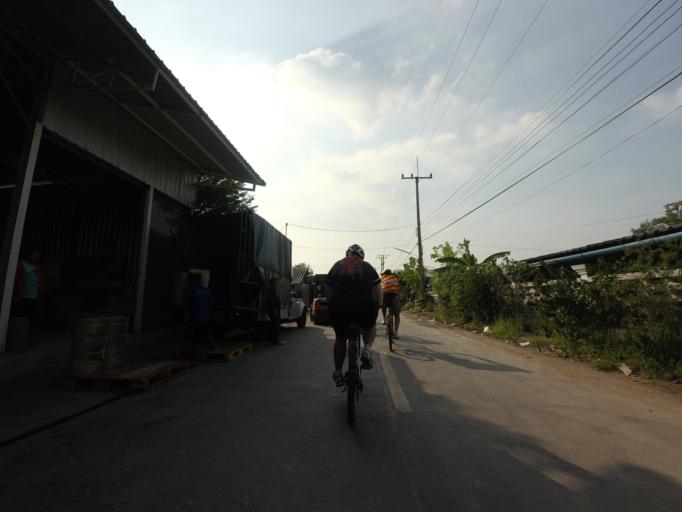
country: TH
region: Samut Sakhon
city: Samut Sakhon
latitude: 13.5080
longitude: 100.3109
